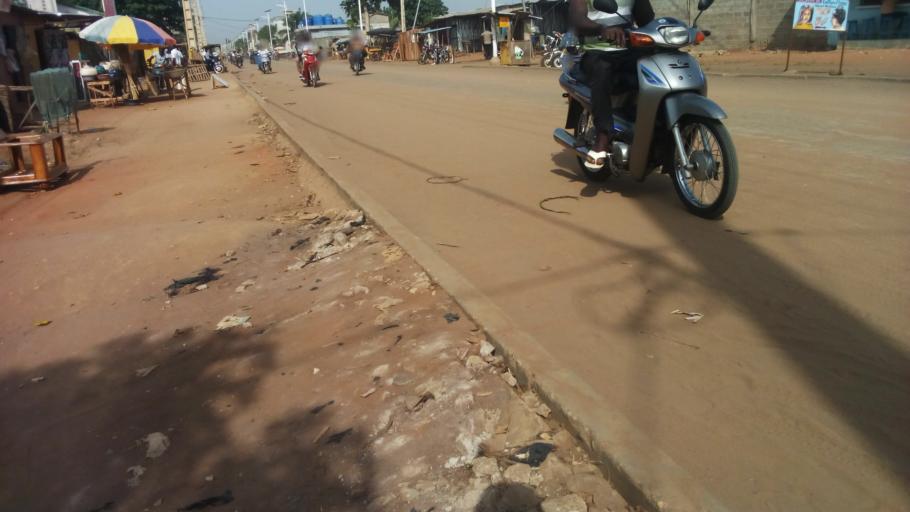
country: BJ
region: Atlantique
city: Abomey-Calavi
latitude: 6.4280
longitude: 2.3264
